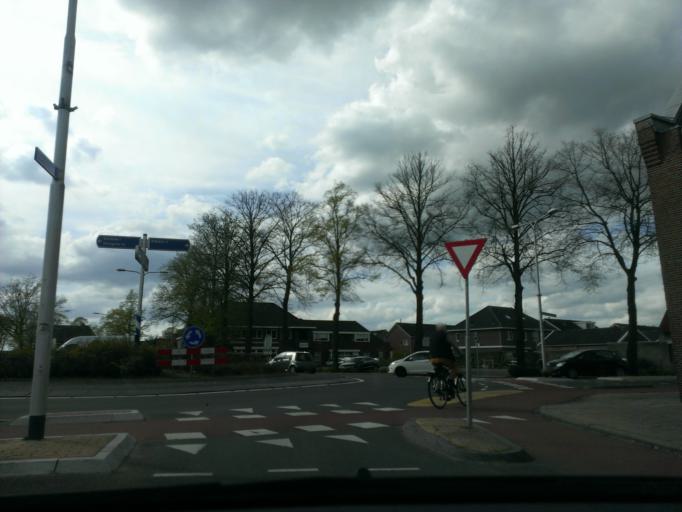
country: NL
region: Overijssel
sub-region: Gemeente Almelo
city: Almelo
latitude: 52.3084
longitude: 6.6558
